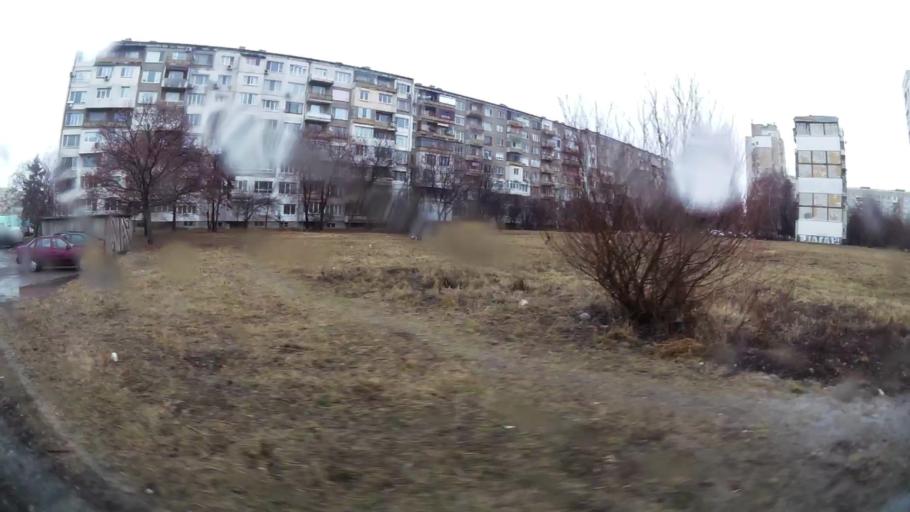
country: BG
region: Sofia-Capital
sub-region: Stolichna Obshtina
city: Sofia
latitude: 42.6539
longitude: 23.3696
